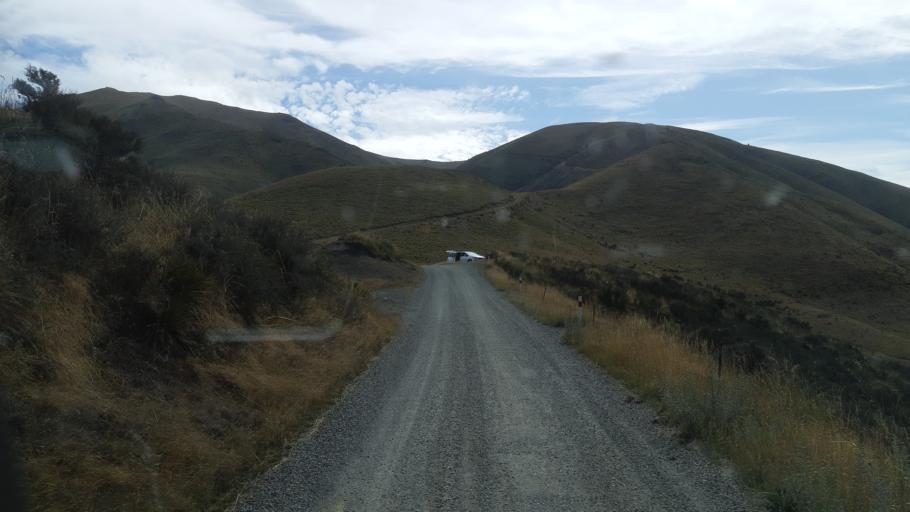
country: NZ
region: Canterbury
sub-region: Timaru District
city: Pleasant Point
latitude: -44.1935
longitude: 170.6097
